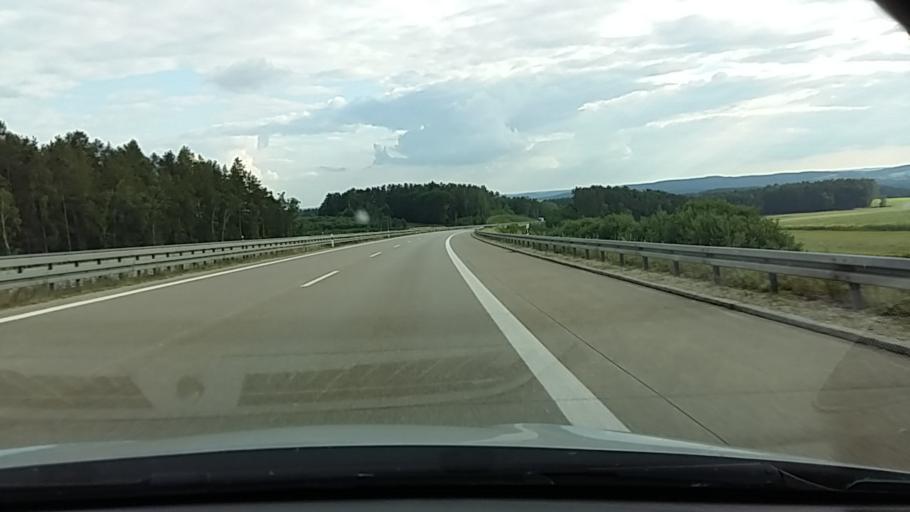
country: DE
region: Bavaria
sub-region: Upper Palatinate
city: Stulln
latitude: 49.4577
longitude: 12.1311
